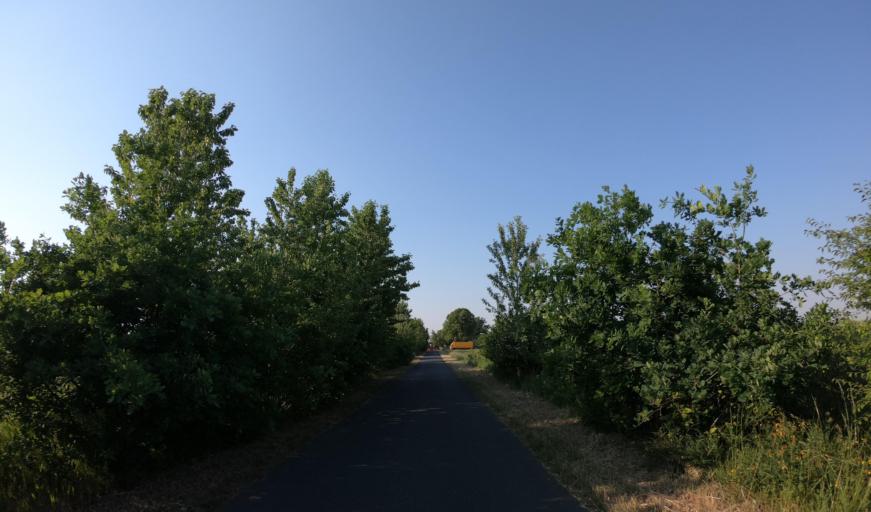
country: PL
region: West Pomeranian Voivodeship
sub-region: Powiat lobeski
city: Radowo Male
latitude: 53.6539
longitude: 15.4115
